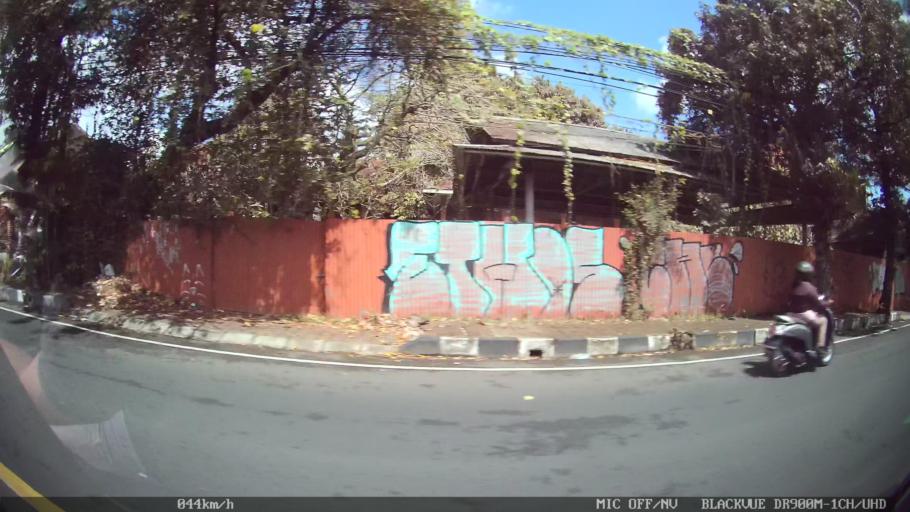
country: ID
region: Bali
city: Banjar Sedang
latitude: -8.5607
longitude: 115.2731
